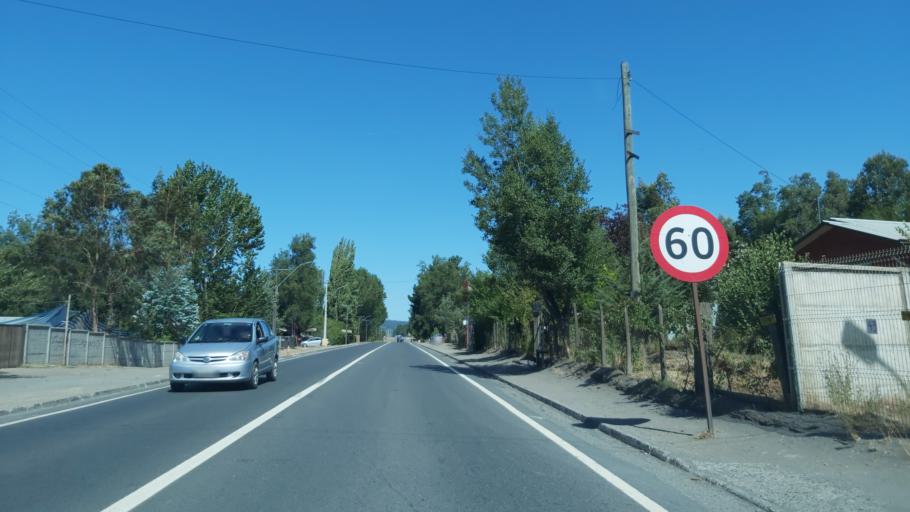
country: CL
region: Biobio
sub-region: Provincia de Concepcion
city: Lota
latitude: -37.1530
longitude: -72.9742
